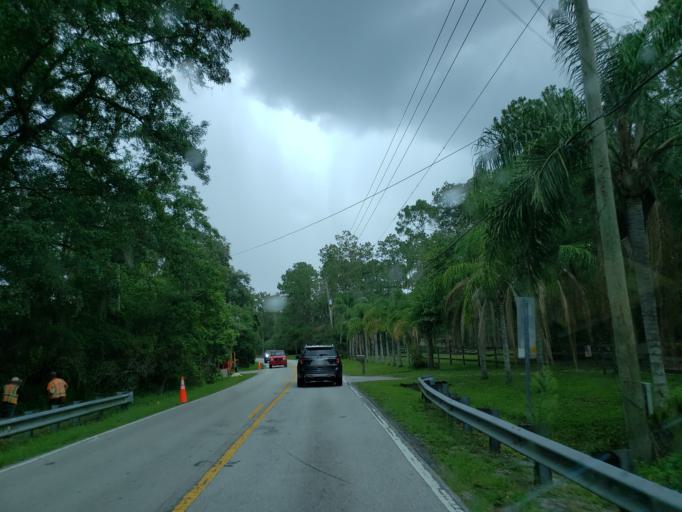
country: US
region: Florida
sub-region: Pasco County
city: Wesley Chapel
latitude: 28.2567
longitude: -82.3543
